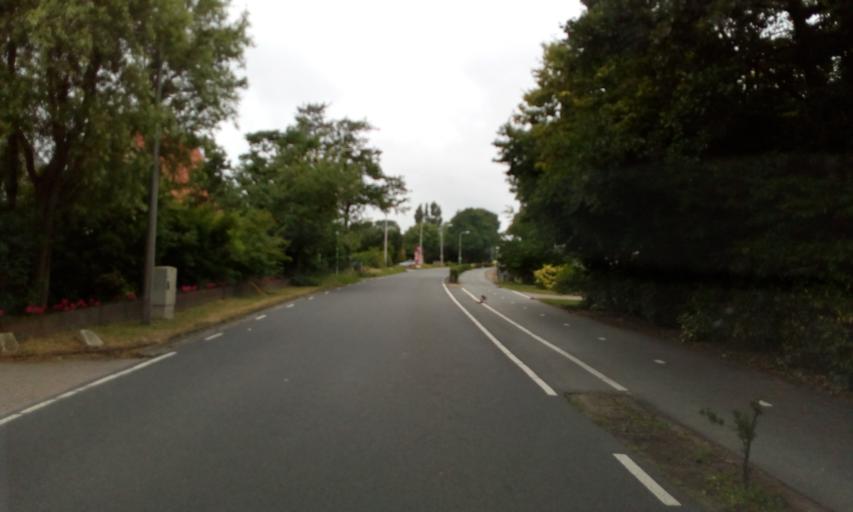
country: NL
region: South Holland
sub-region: Gemeente Westland
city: Poeldijk
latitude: 52.0326
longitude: 4.2000
